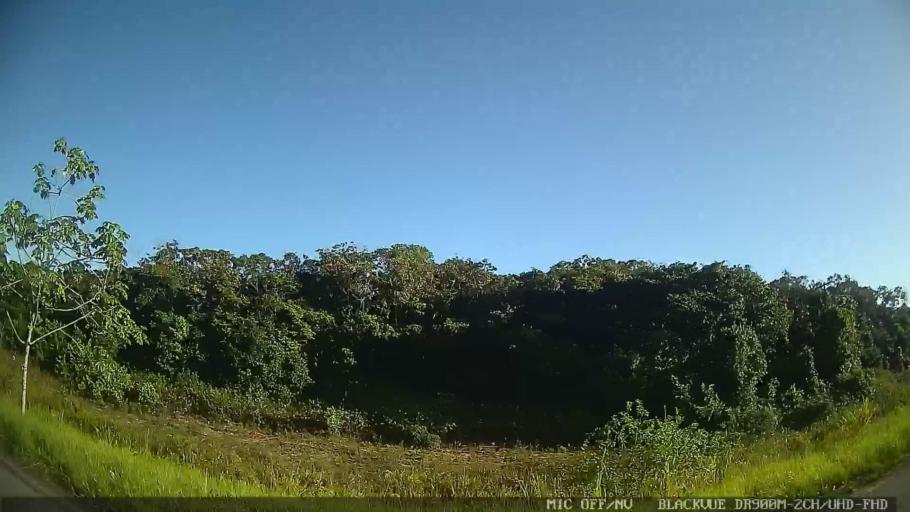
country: BR
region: Sao Paulo
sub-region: Itanhaem
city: Itanhaem
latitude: -24.1956
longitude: -46.8380
